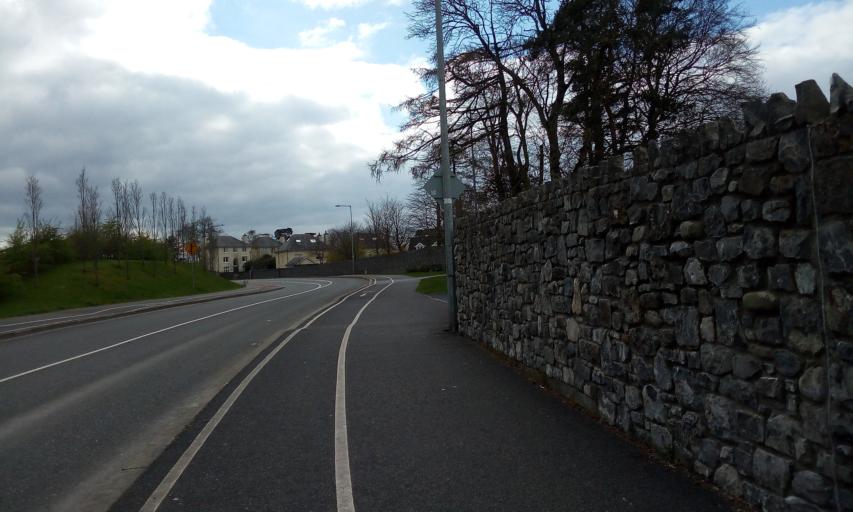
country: IE
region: Leinster
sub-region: Kilkenny
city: Kilkenny
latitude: 52.6415
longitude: -7.2557
